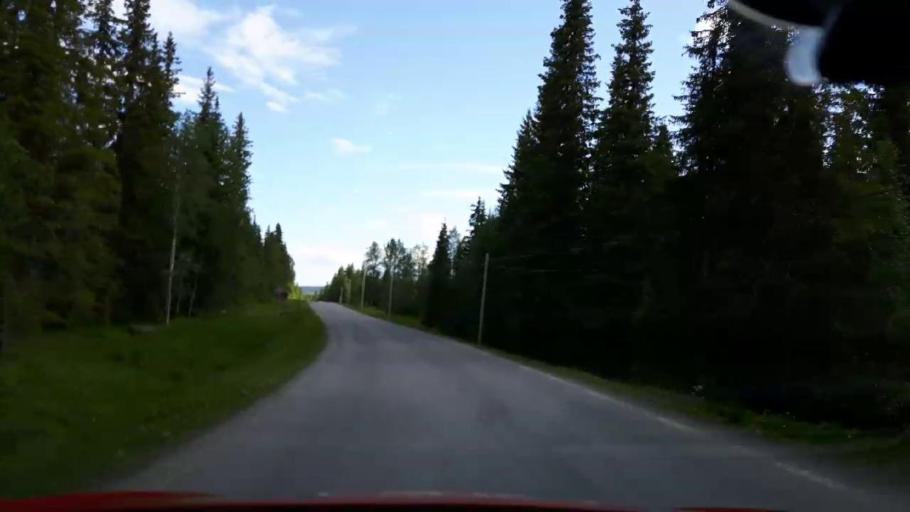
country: SE
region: Jaemtland
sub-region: Krokoms Kommun
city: Valla
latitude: 63.7779
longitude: 14.0434
